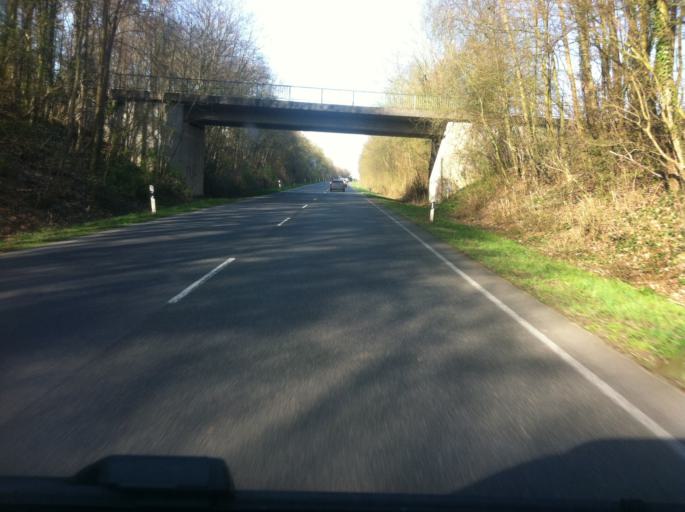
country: DE
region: North Rhine-Westphalia
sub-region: Regierungsbezirk Koln
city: Norvenich
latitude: 50.7561
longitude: 6.6516
